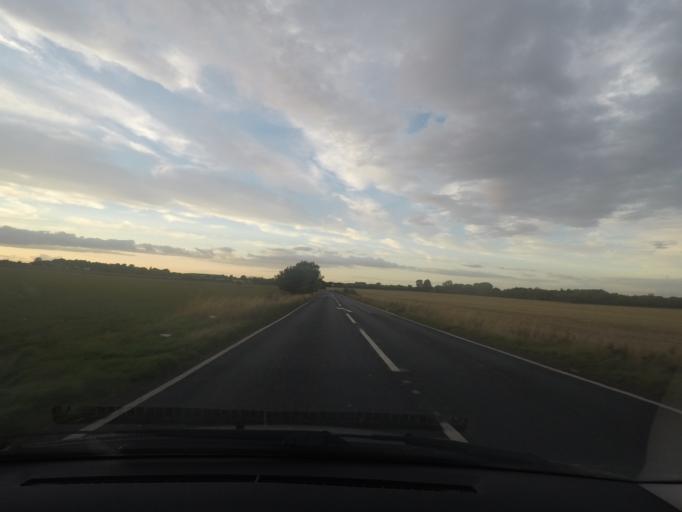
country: GB
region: England
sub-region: North East Lincolnshire
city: Laceby
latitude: 53.5215
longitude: -0.1623
